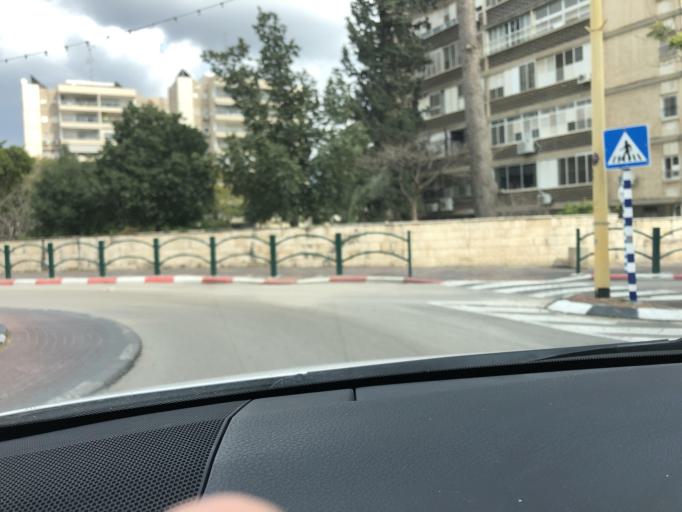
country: IL
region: Central District
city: Ganne Tiqwa
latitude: 32.0605
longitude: 34.8680
